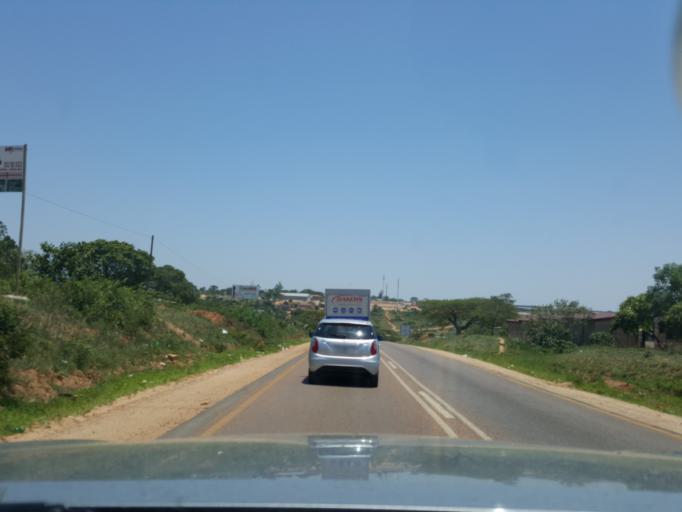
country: ZA
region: Limpopo
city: Thulamahashi
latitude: -24.6174
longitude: 31.0392
